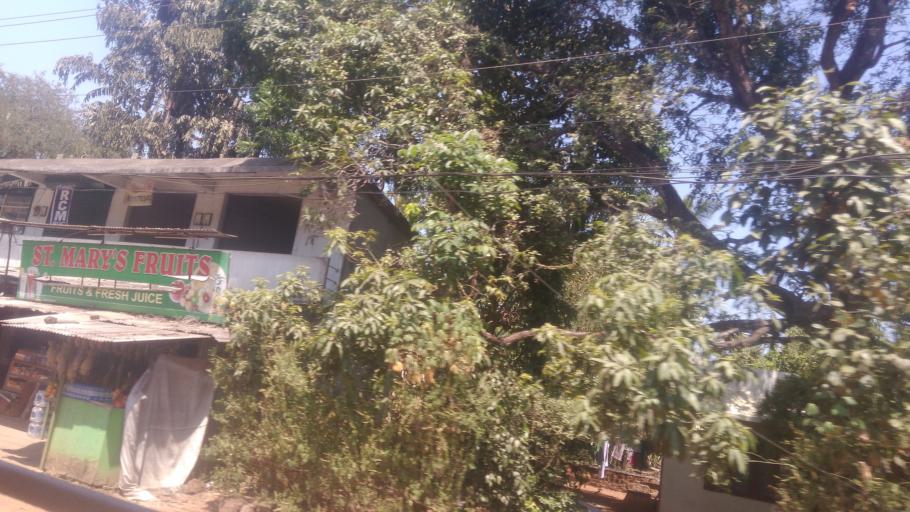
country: IN
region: Kerala
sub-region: Kottayam
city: Kottayam
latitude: 9.5898
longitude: 76.5800
